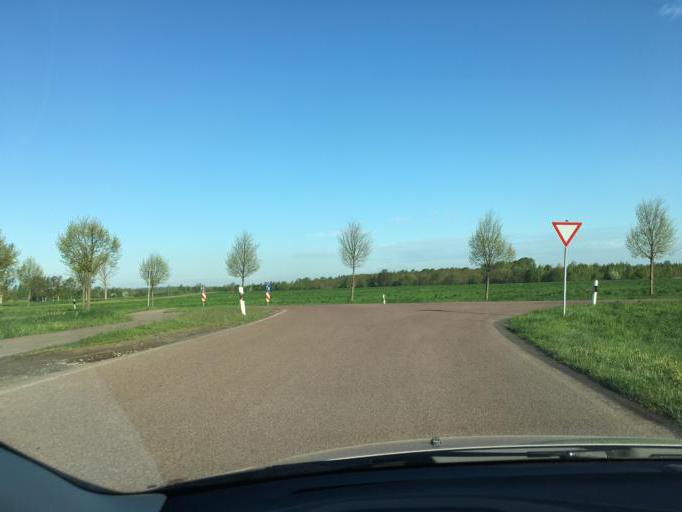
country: DE
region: Saxony
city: Espenhain
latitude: 51.2163
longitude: 12.4562
